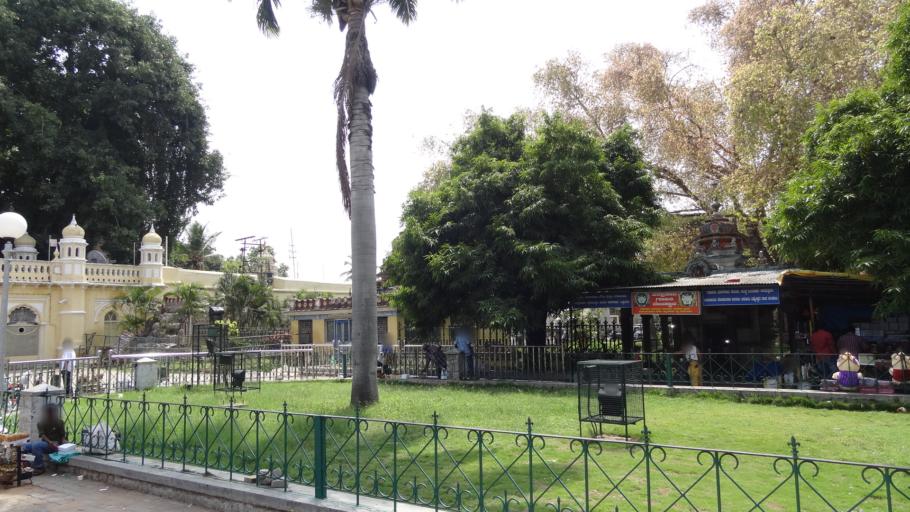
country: IN
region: Karnataka
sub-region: Mysore
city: Mysore
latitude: 12.3032
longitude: 76.6553
